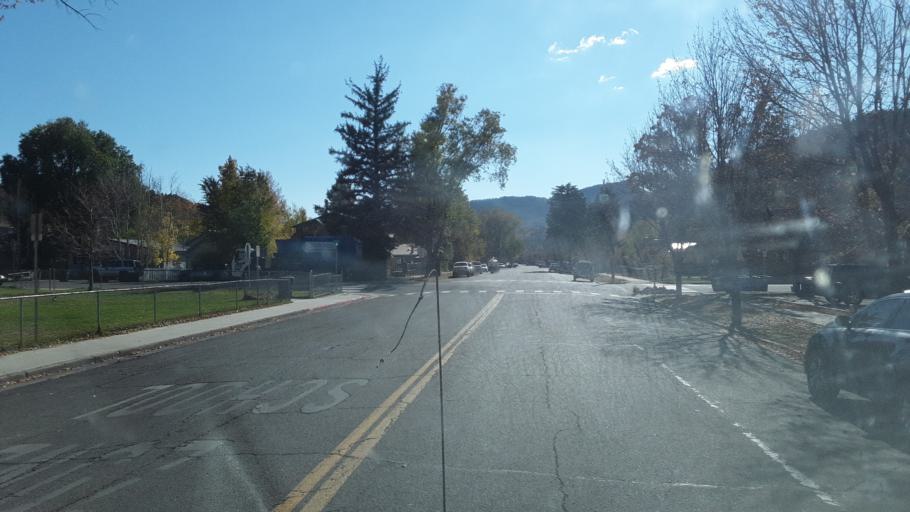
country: US
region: Colorado
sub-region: La Plata County
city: Durango
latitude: 37.2671
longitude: -107.8755
